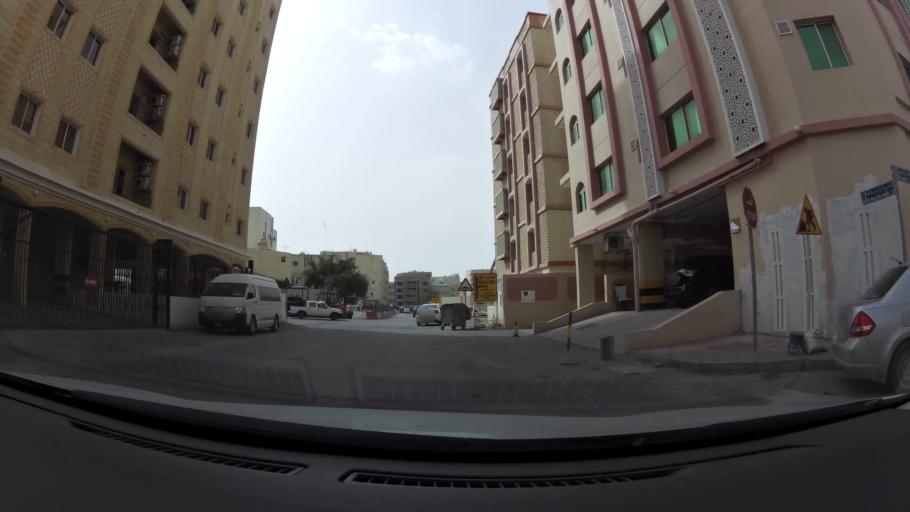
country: QA
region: Baladiyat ad Dawhah
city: Doha
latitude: 25.2713
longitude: 51.5358
